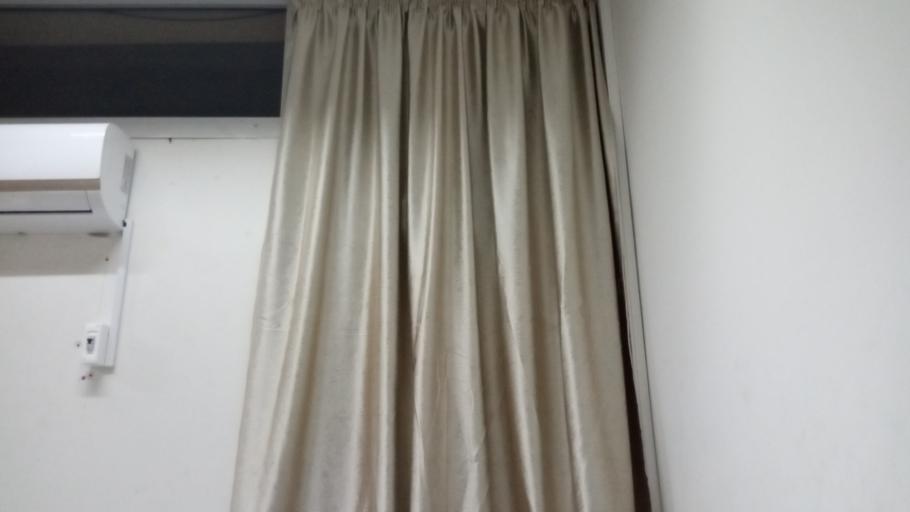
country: CI
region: Lagunes
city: Abidjan
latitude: 5.3431
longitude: -3.9868
